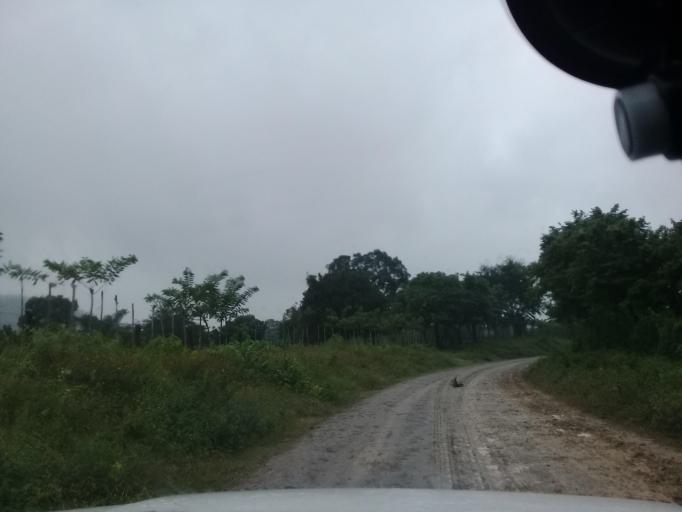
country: MX
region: Veracruz
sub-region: Chalma
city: San Pedro Coyutla
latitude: 21.2451
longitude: -98.4628
